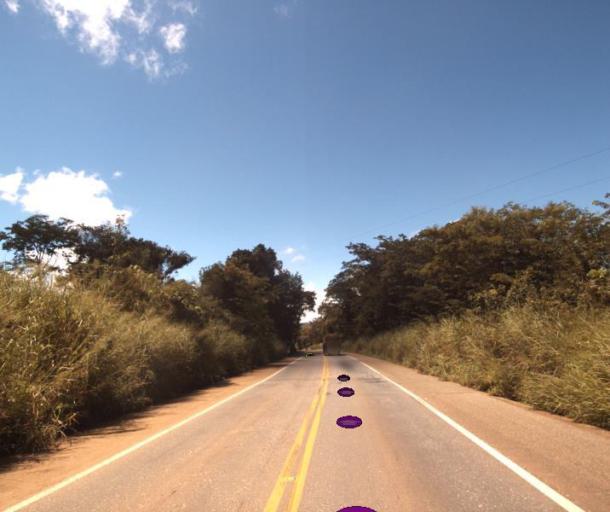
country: BR
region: Goias
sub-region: Pirenopolis
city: Pirenopolis
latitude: -16.0768
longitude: -49.0528
